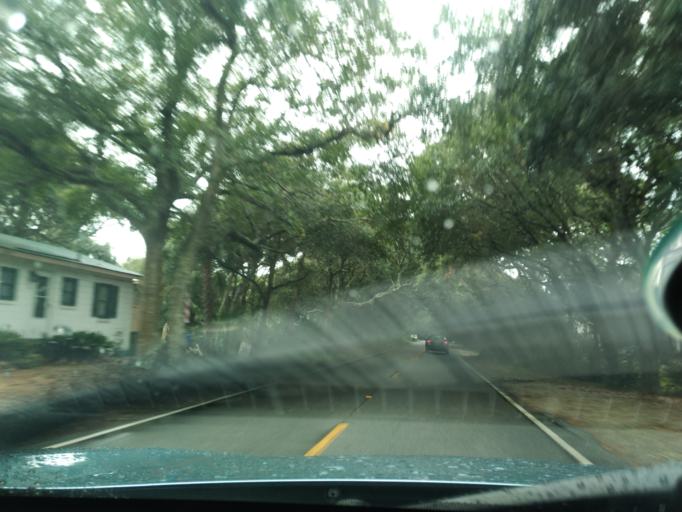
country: US
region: South Carolina
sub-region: Charleston County
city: Folly Beach
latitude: 32.6645
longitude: -79.9199
